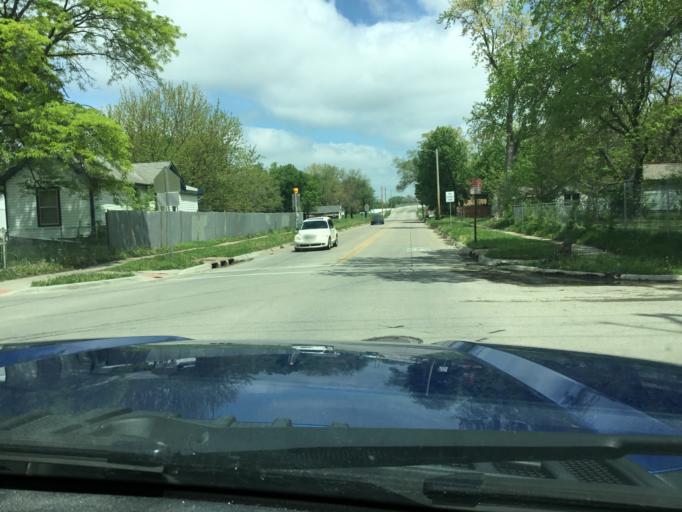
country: US
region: Kansas
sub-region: Shawnee County
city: Topeka
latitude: 39.0489
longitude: -95.6437
